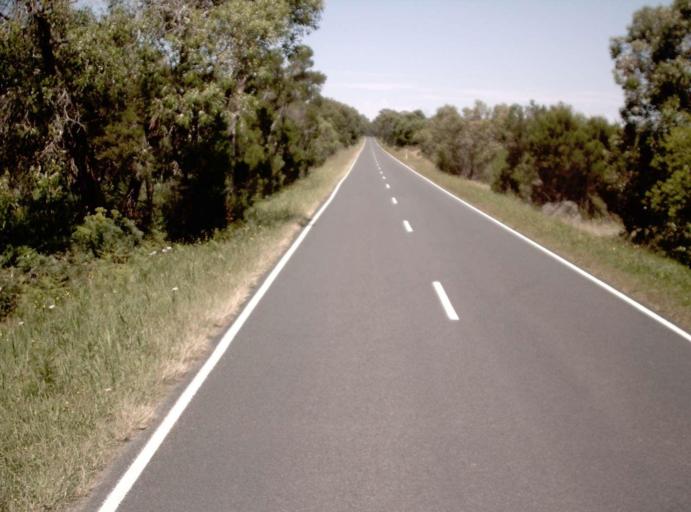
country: AU
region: Victoria
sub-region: Bass Coast
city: North Wonthaggi
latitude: -38.5909
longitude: 145.9771
